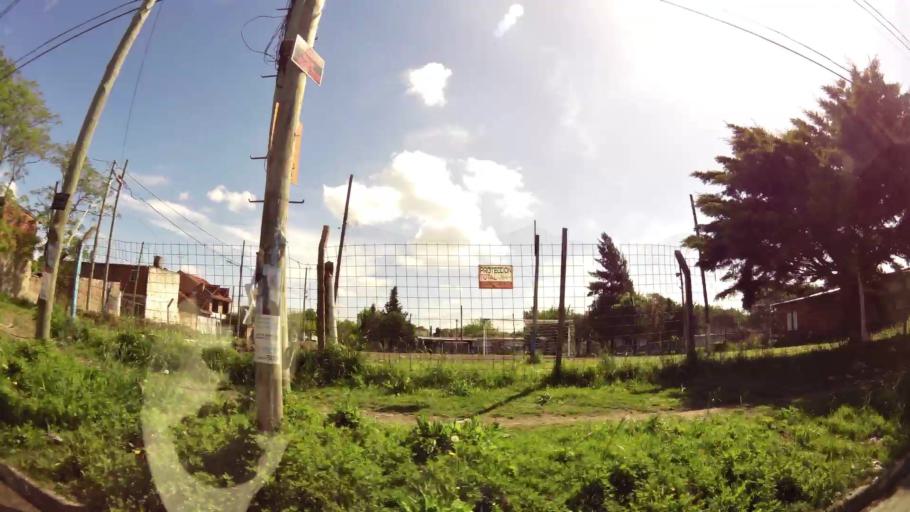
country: AR
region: Buenos Aires
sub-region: Partido de Quilmes
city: Quilmes
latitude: -34.8023
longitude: -58.2658
